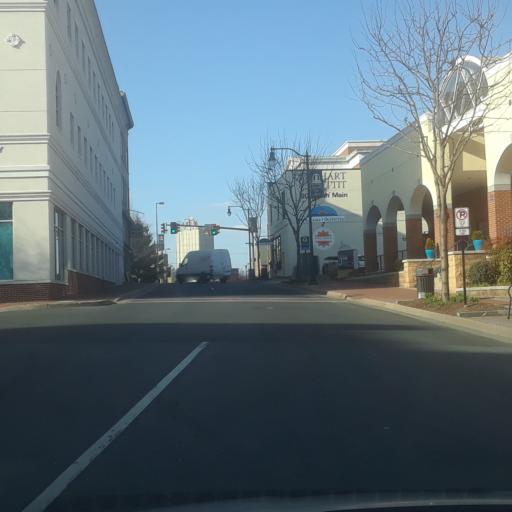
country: US
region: Virginia
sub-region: City of Harrisonburg
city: Harrisonburg
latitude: 38.4495
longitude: -78.8686
